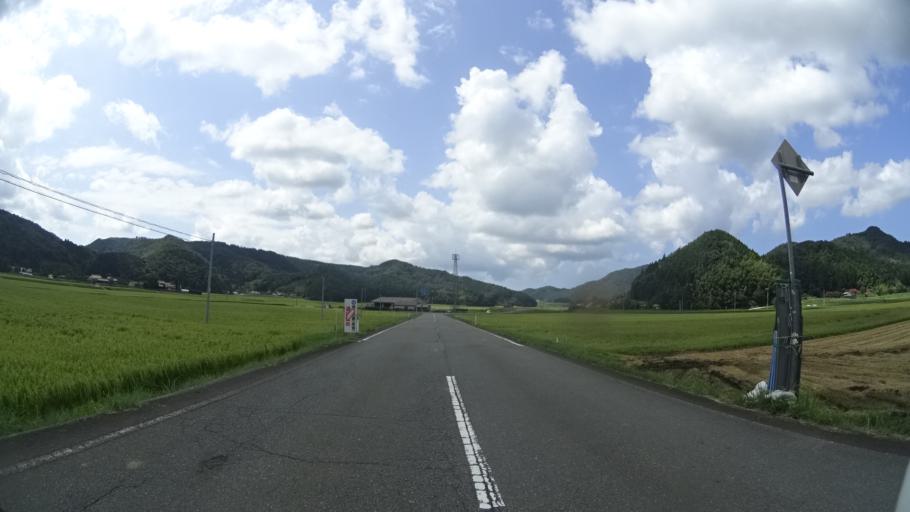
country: JP
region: Yamaguchi
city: Hagi
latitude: 34.5168
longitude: 131.6106
